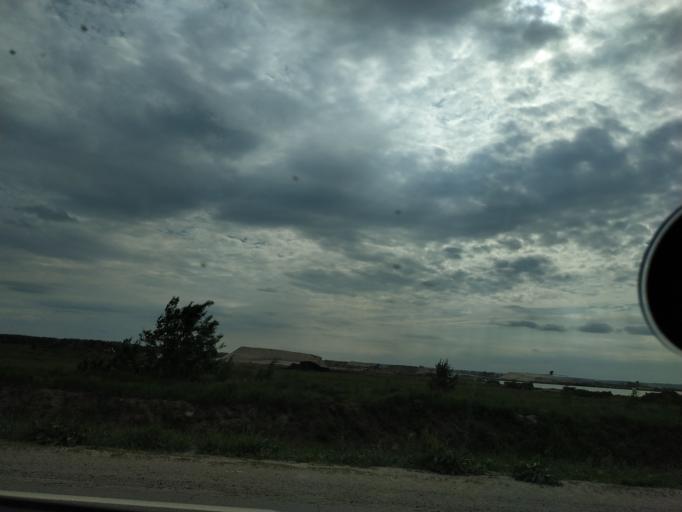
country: RU
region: Moskovskaya
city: Malyshevo
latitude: 55.5067
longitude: 38.2891
